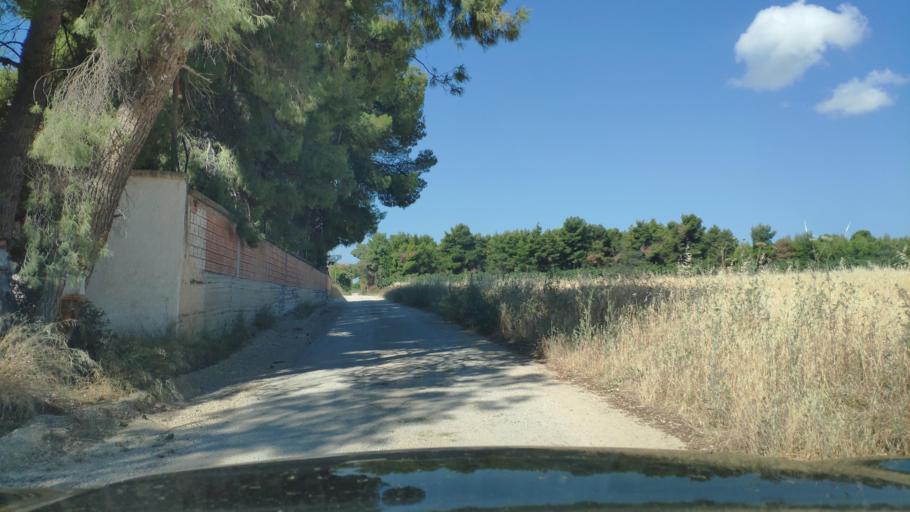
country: GR
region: Central Greece
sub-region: Nomos Voiotias
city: Arma
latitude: 38.3989
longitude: 23.5135
